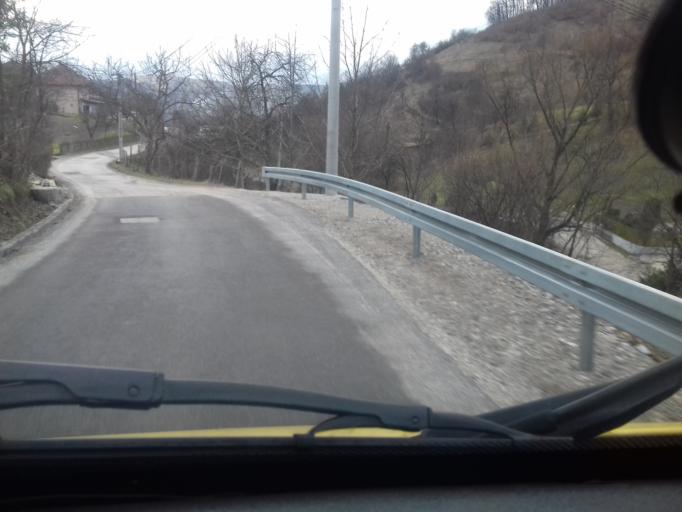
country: BA
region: Federation of Bosnia and Herzegovina
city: Zenica
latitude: 44.2401
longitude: 17.9146
